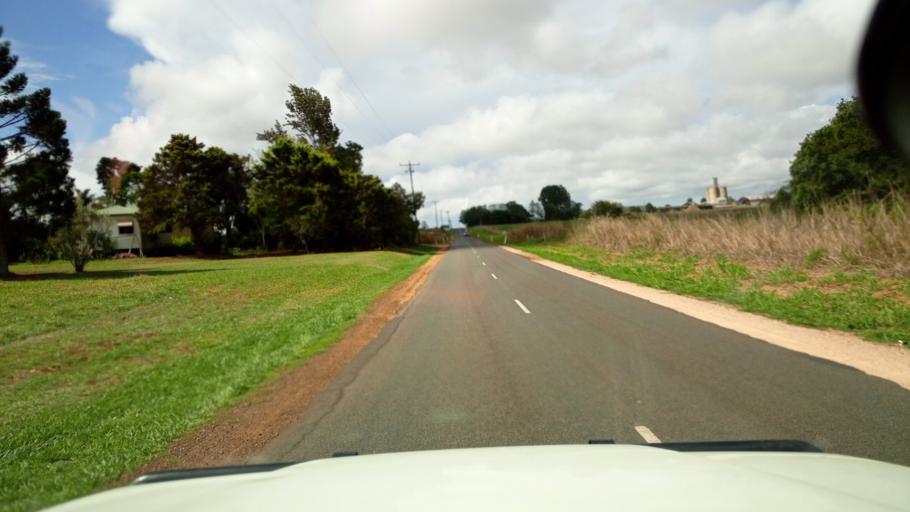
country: AU
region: Queensland
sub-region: Tablelands
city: Tolga
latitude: -17.2221
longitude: 145.5376
